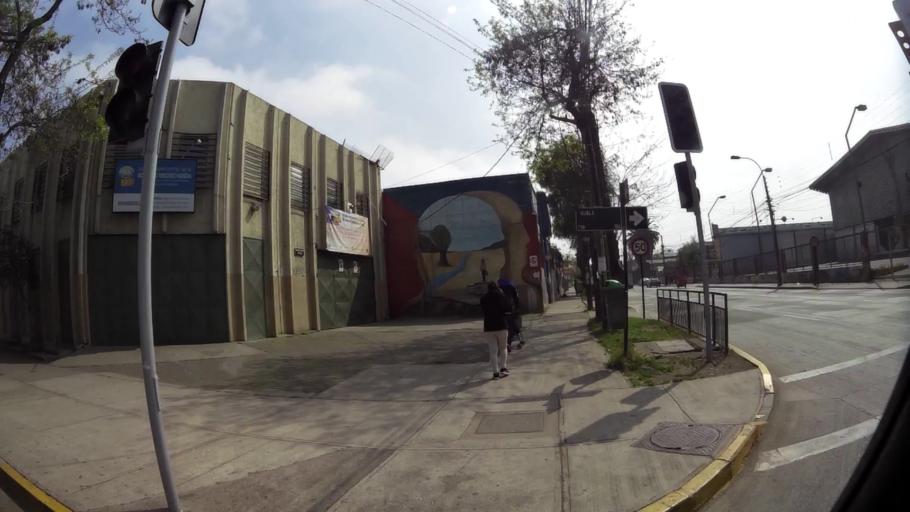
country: CL
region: Santiago Metropolitan
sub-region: Provincia de Santiago
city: Santiago
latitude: -33.4691
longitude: -70.6423
